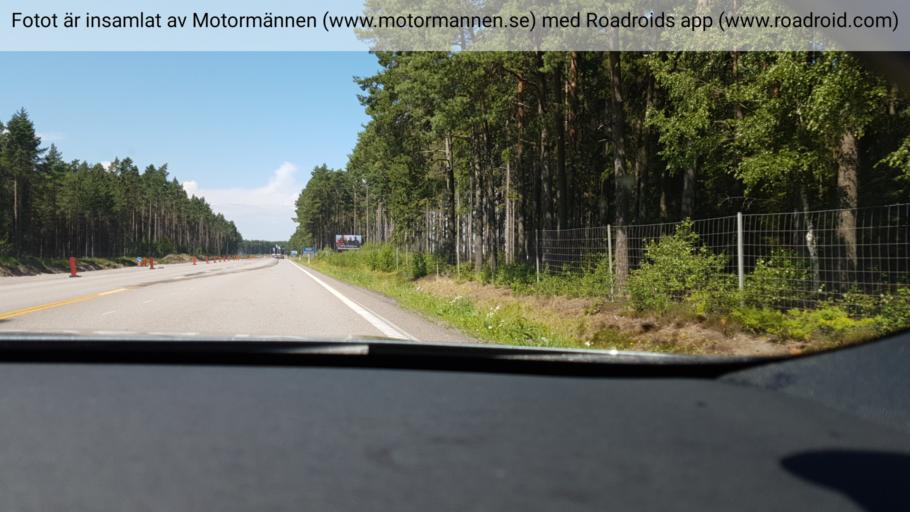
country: SE
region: Vaestra Goetaland
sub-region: Lidkopings Kommun
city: Lidkoping
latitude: 58.4825
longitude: 13.1975
